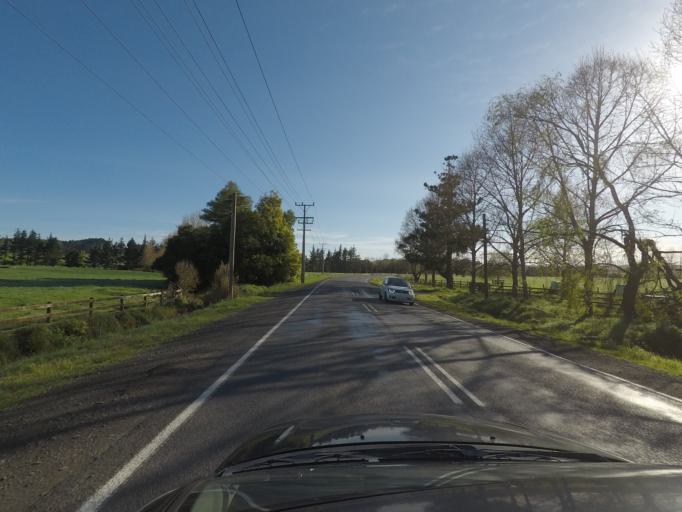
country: NZ
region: Auckland
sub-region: Auckland
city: Red Hill
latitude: -37.0036
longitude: 174.9566
